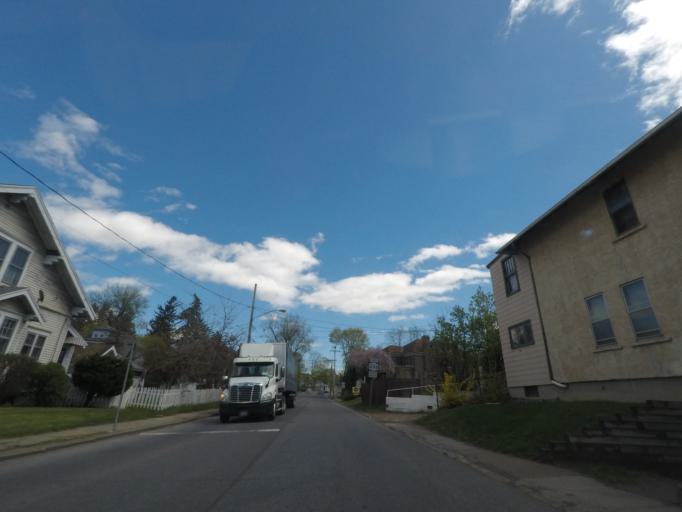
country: US
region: New York
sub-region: Columbia County
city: Oakdale
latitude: 42.2473
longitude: -73.7731
